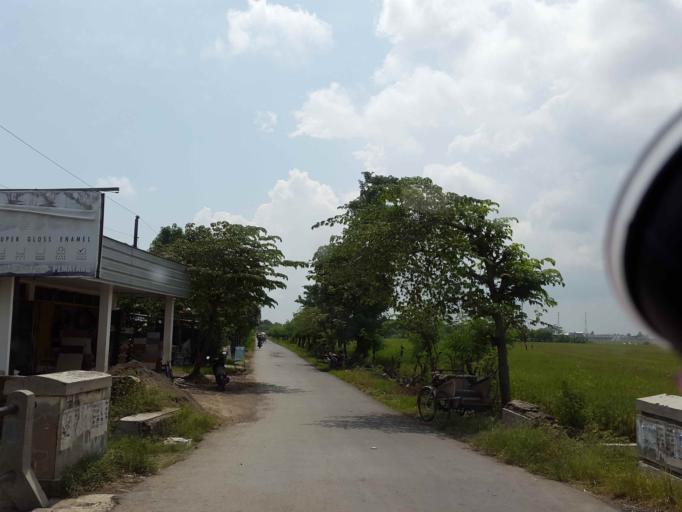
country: ID
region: Central Java
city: Pemalang
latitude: -6.9016
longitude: 109.3699
